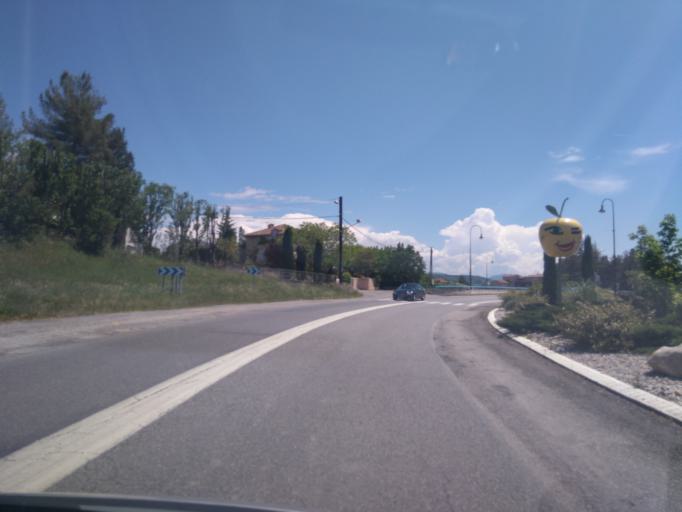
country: FR
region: Provence-Alpes-Cote d'Azur
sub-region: Departement des Hautes-Alpes
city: Laragne-Monteglin
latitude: 44.3178
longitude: 5.8133
